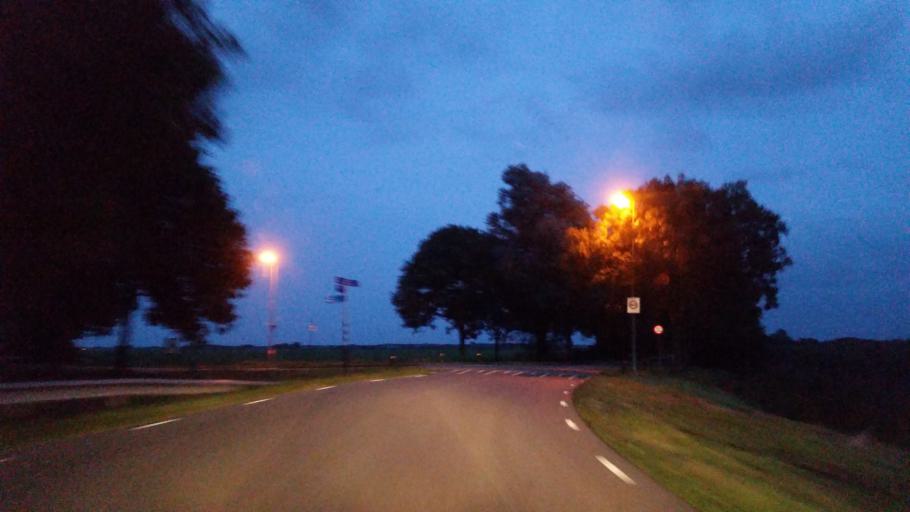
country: NL
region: Friesland
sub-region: Gemeente Leeuwarden
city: Camminghaburen
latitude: 53.2405
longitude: 5.8454
